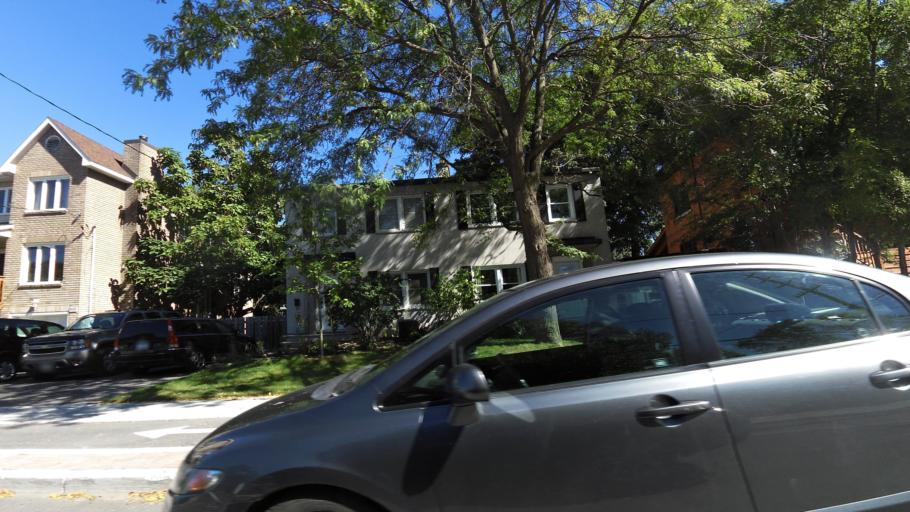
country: CA
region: Ontario
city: Ottawa
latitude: 45.3860
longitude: -75.7501
